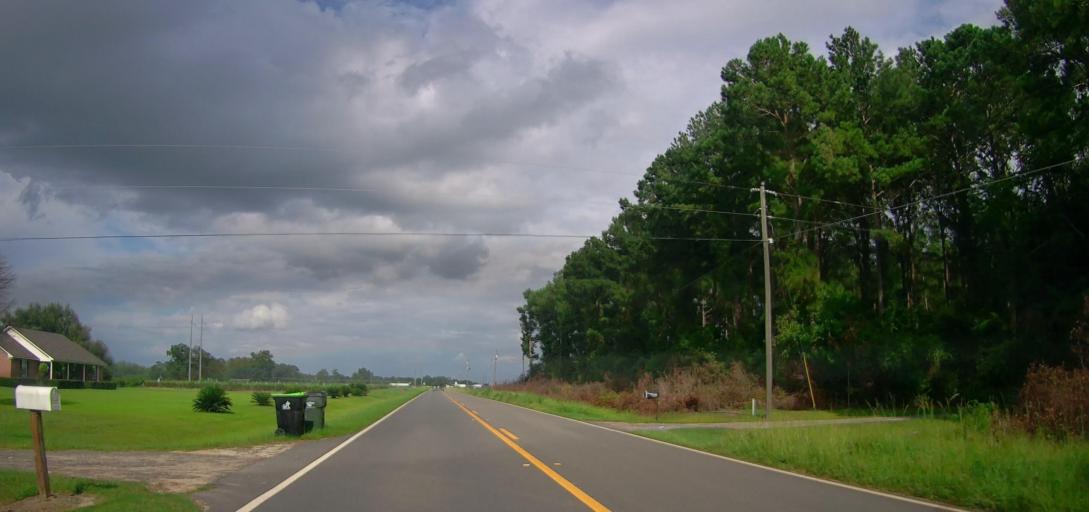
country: US
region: Georgia
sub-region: Coffee County
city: Douglas
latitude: 31.4539
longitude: -82.8577
